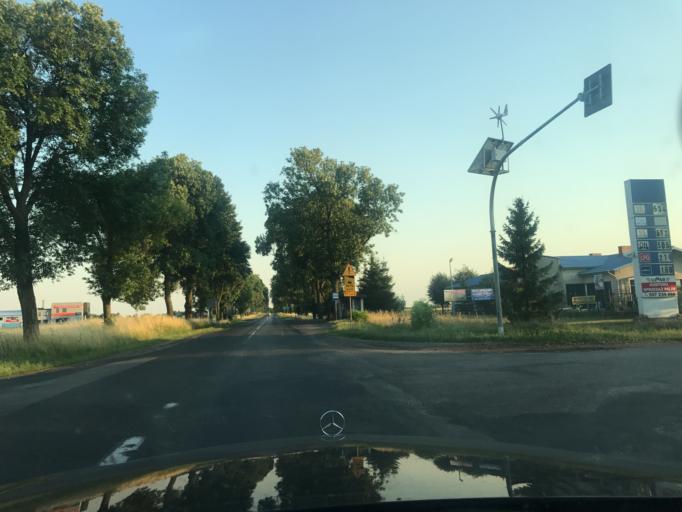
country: PL
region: Lublin Voivodeship
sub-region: Powiat lubartowski
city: Niedzwiada
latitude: 51.5121
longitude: 22.6659
